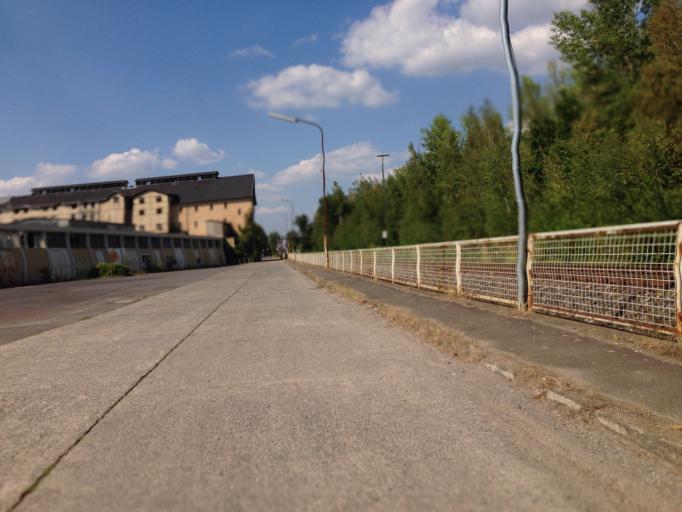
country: DE
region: Hesse
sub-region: Regierungsbezirk Giessen
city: Giessen
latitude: 50.5668
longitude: 8.6867
